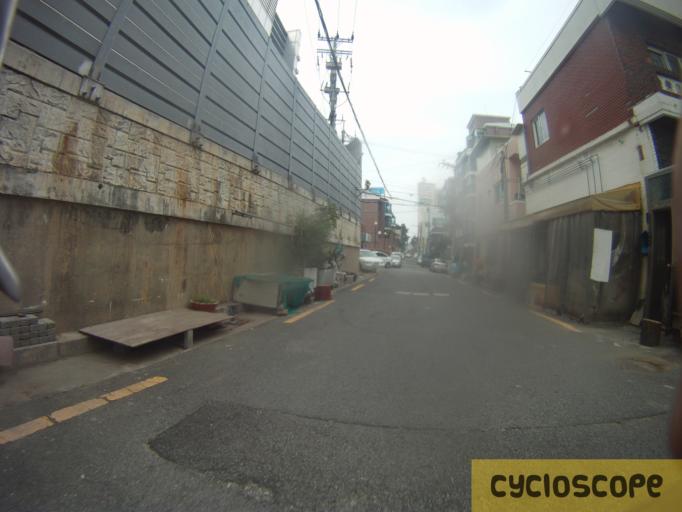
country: KR
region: Busan
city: Kijang
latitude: 35.1797
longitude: 129.1969
